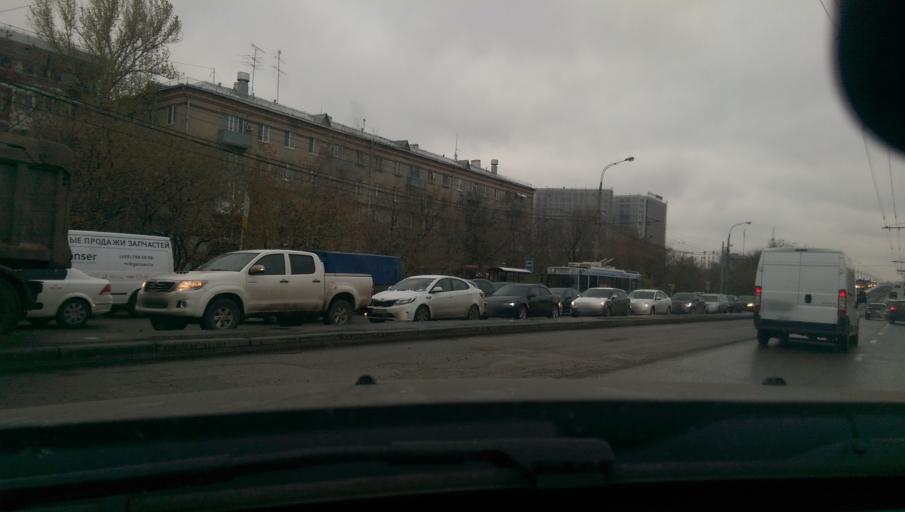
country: RU
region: Moskovskaya
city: Fili
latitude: 55.7511
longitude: 37.5087
